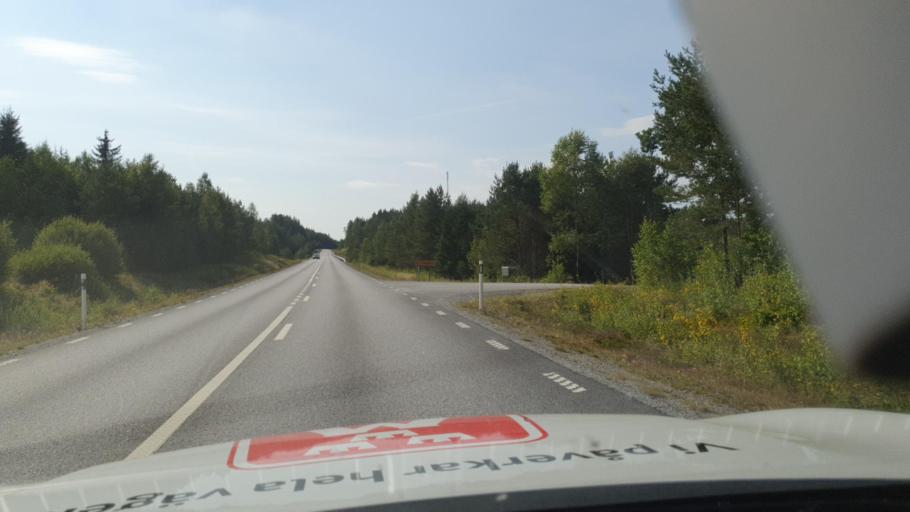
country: SE
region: Vaestra Goetaland
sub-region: Tanums Kommun
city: Tanumshede
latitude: 58.8130
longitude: 11.5992
